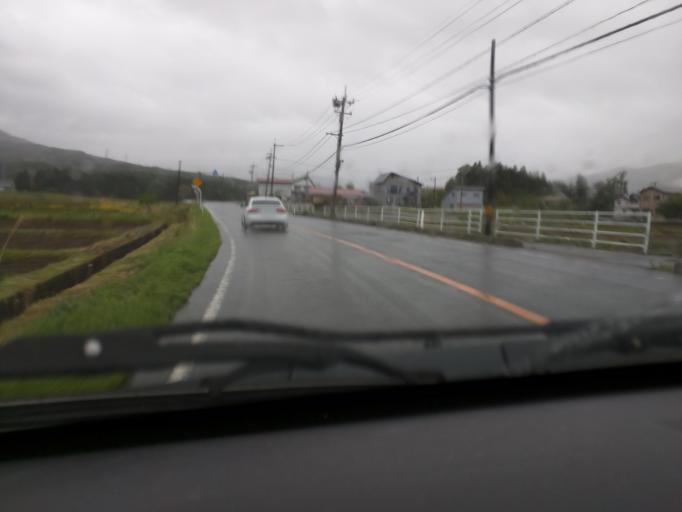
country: JP
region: Fukushima
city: Inawashiro
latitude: 37.5687
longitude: 140.1153
